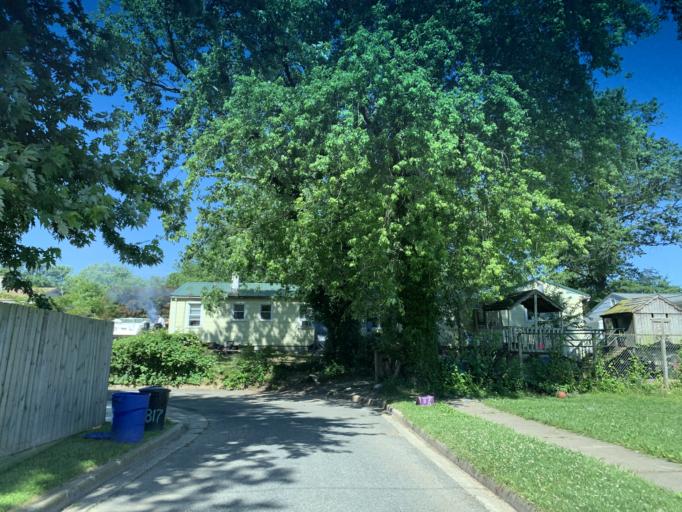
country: US
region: Maryland
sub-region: Harford County
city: Havre de Grace
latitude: 39.5410
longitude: -76.0984
